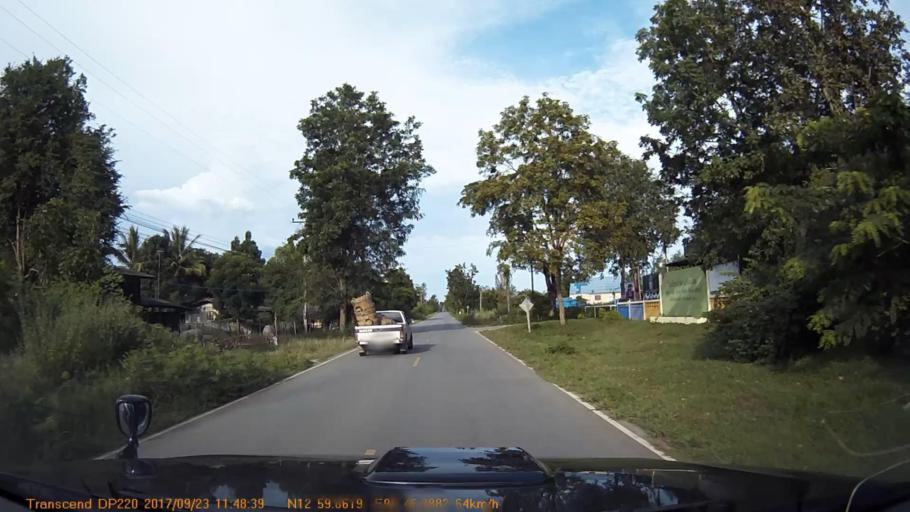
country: TH
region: Phetchaburi
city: Tha Yang
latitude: 12.9944
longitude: 99.7815
